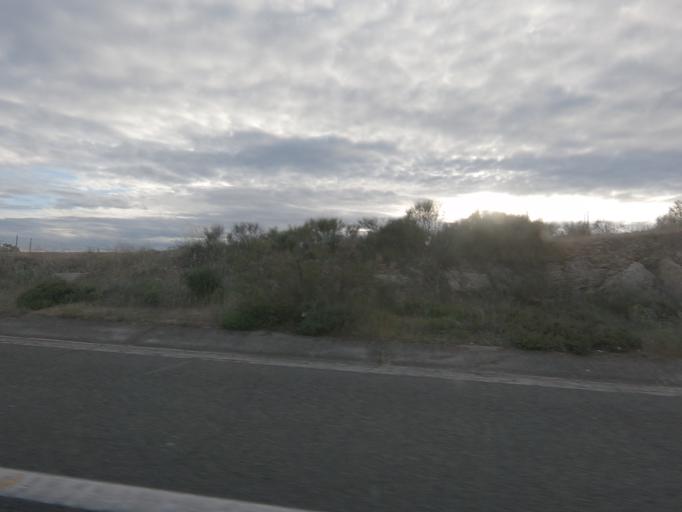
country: ES
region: Extremadura
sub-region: Provincia de Caceres
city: Casar de Caceres
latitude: 39.4973
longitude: -6.4381
